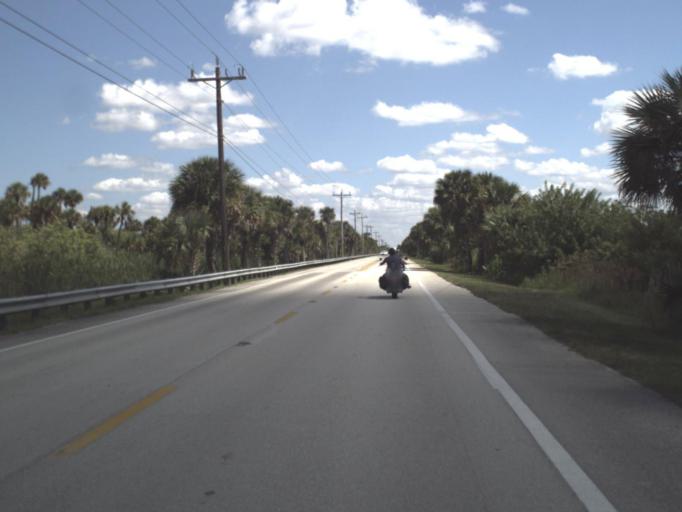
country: US
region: Florida
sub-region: Collier County
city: Marco
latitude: 25.9308
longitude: -81.4401
